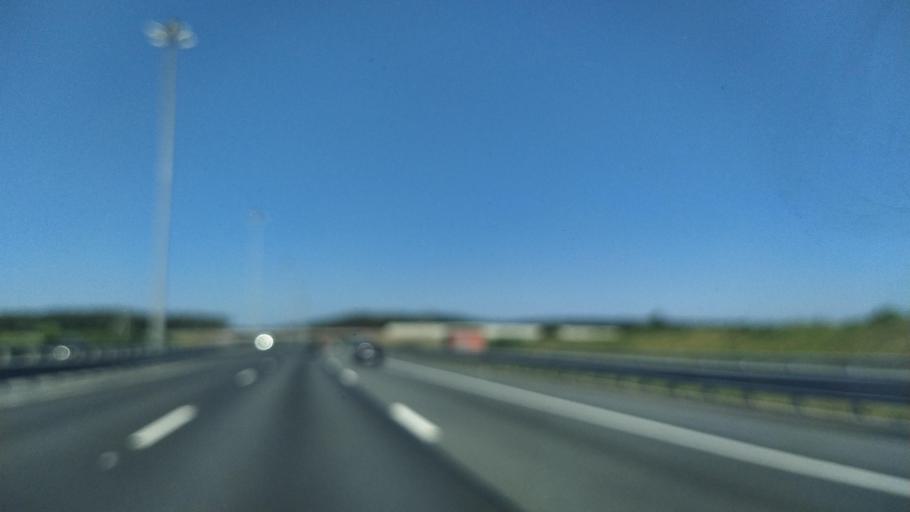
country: RU
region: Leningrad
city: Gorbunki
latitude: 59.8187
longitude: 30.0004
